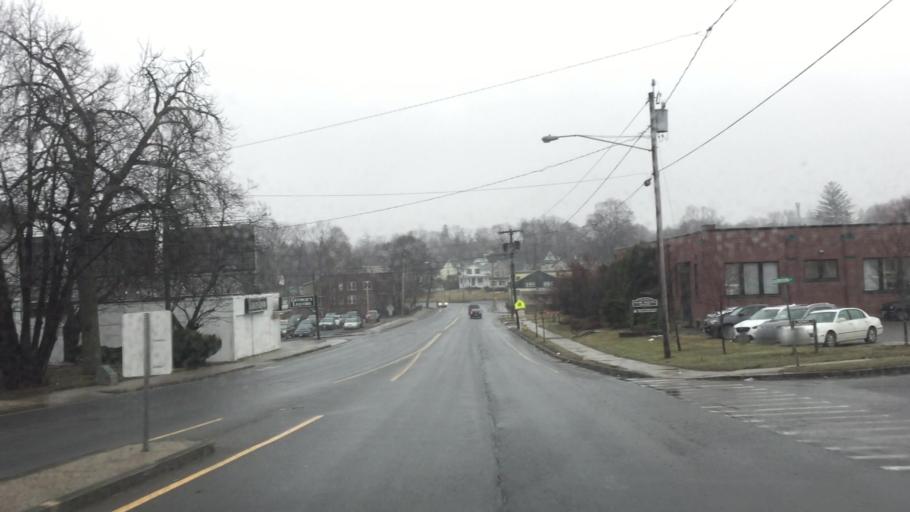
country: US
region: Massachusetts
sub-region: Berkshire County
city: Pittsfield
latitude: 42.4466
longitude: -73.2449
